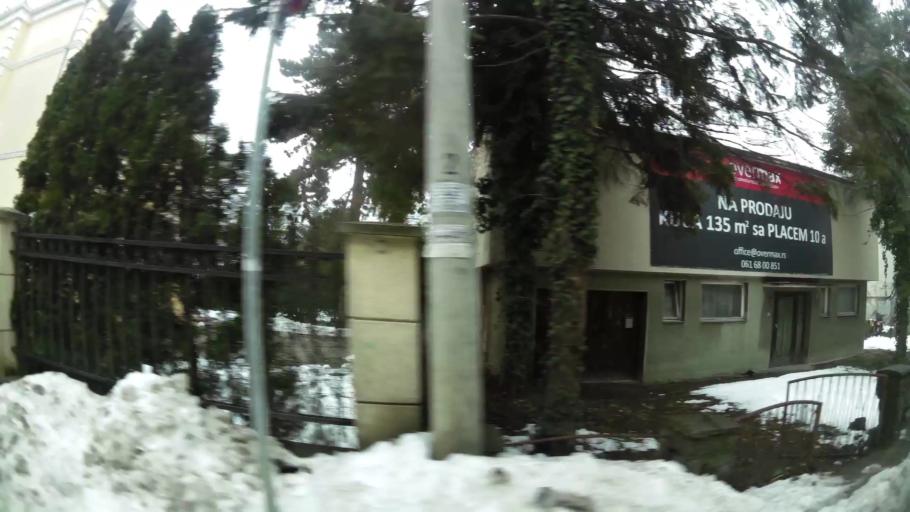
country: RS
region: Central Serbia
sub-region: Belgrade
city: Savski Venac
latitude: 44.7775
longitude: 20.4603
